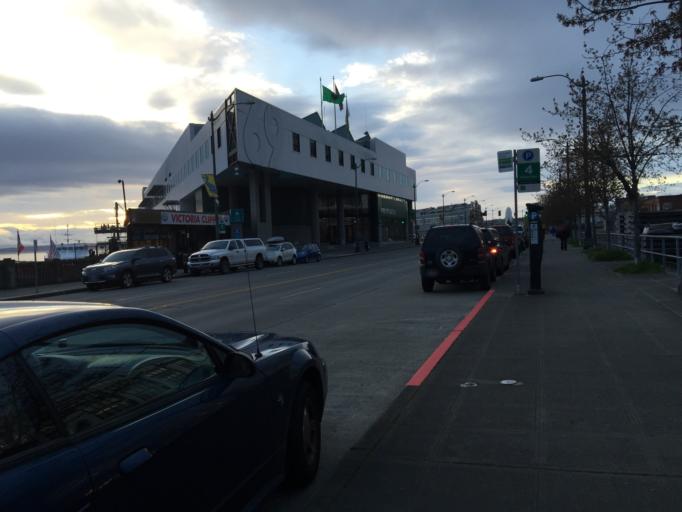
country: US
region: Washington
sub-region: King County
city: Seattle
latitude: 47.6137
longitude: -122.3525
